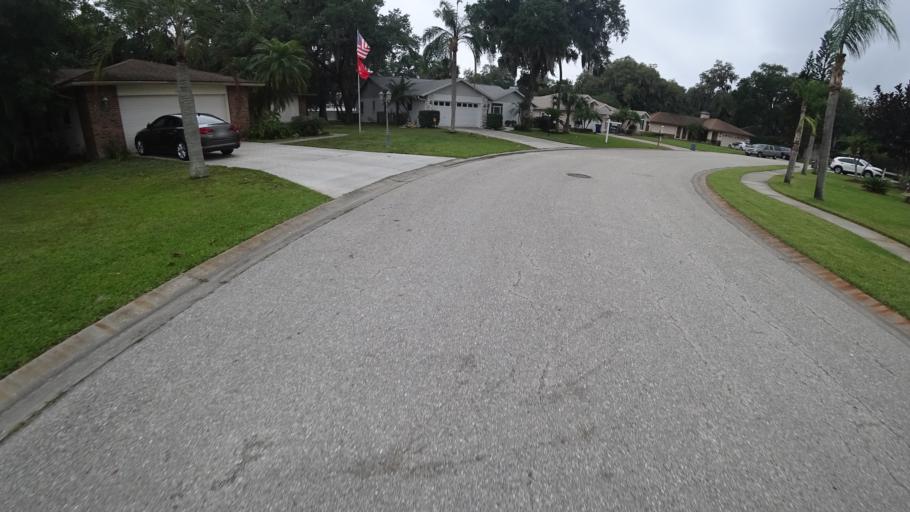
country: US
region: Florida
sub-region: Manatee County
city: Samoset
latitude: 27.4368
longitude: -82.5124
